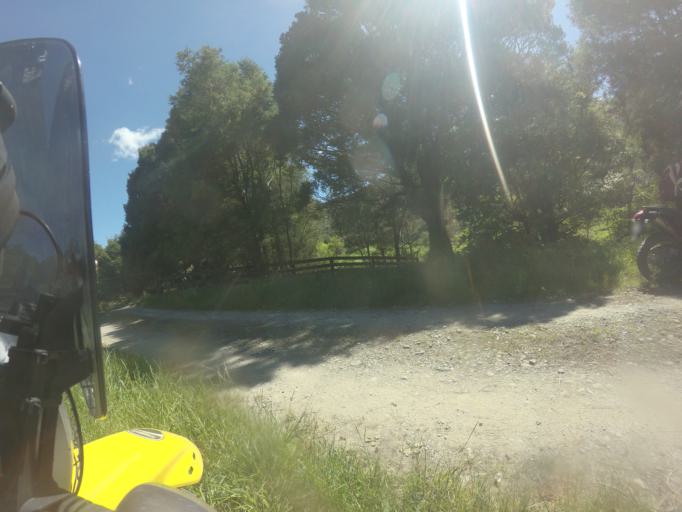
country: NZ
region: Bay of Plenty
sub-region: Opotiki District
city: Opotiki
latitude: -38.3013
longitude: 177.3347
